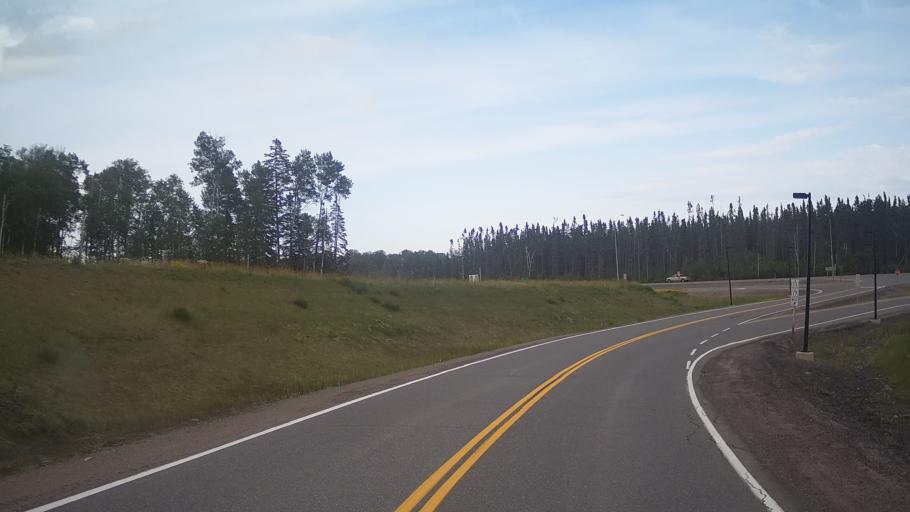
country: CA
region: Ontario
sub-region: Thunder Bay District
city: Thunder Bay
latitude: 48.4883
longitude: -89.1587
